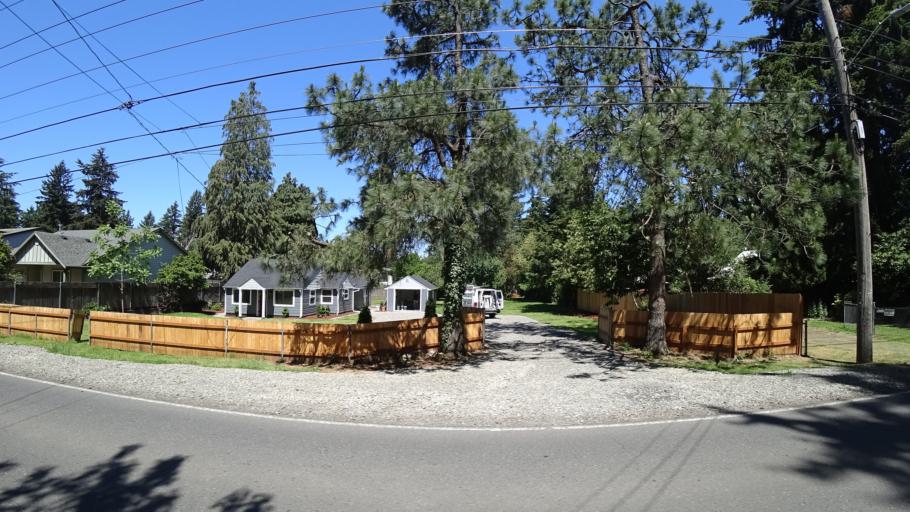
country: US
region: Oregon
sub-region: Multnomah County
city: Lents
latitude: 45.4833
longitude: -122.5341
